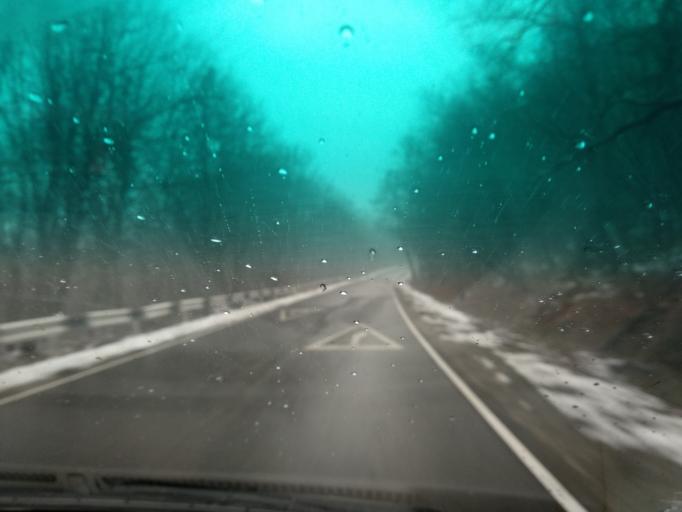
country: RU
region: Krasnodarskiy
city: Khadyzhensk
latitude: 44.2634
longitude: 39.3582
